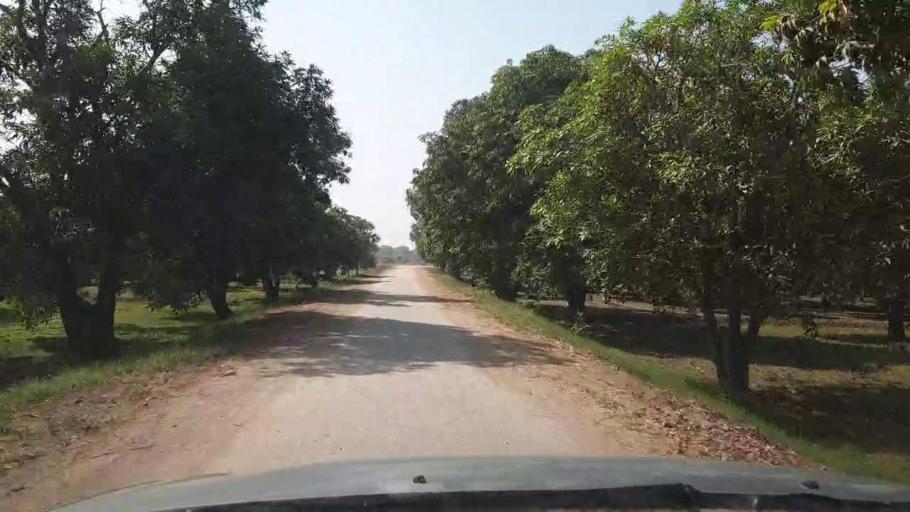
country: PK
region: Sindh
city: Tando Jam
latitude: 25.3613
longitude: 68.5233
